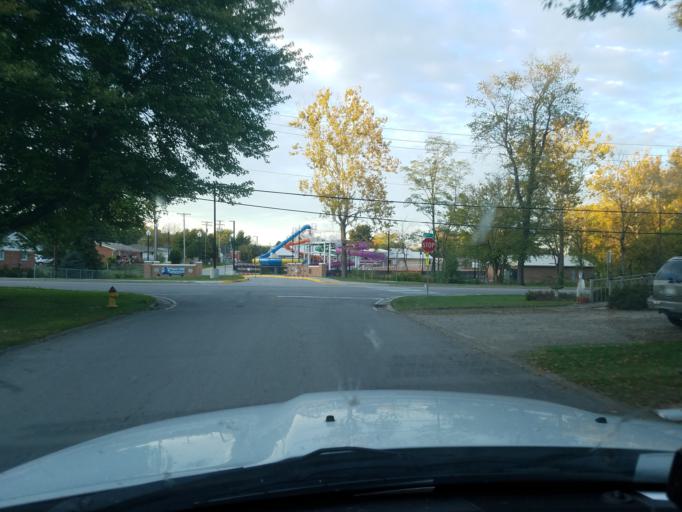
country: US
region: Indiana
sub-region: Floyd County
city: New Albany
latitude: 38.3097
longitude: -85.8408
